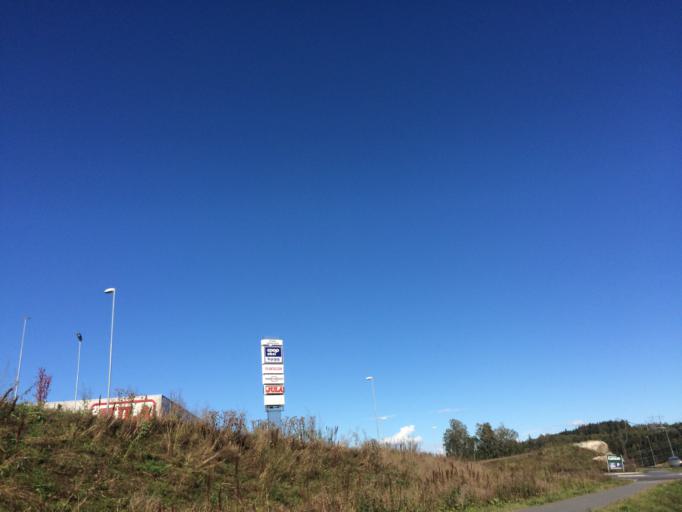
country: NO
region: Akershus
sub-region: Ski
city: Ski
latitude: 59.7247
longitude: 10.7823
